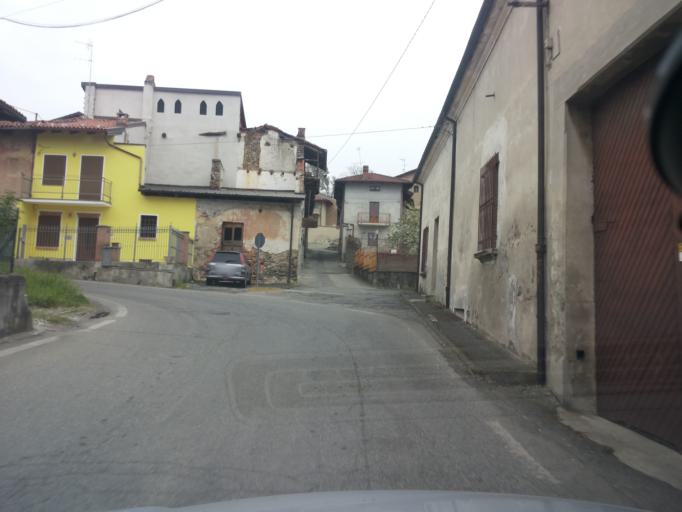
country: IT
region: Piedmont
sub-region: Provincia di Torino
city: Settimo Rottaro
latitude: 45.4047
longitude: 7.9910
